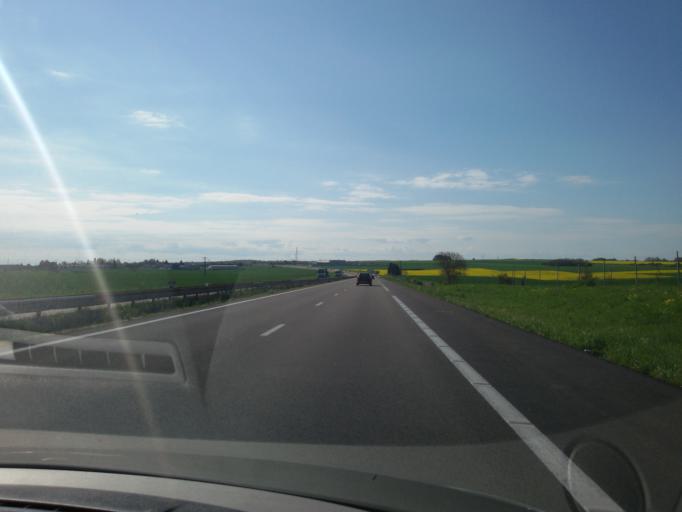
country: FR
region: Bourgogne
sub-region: Departement de l'Yonne
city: Joux-la-Ville
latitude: 47.6718
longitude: 3.8654
